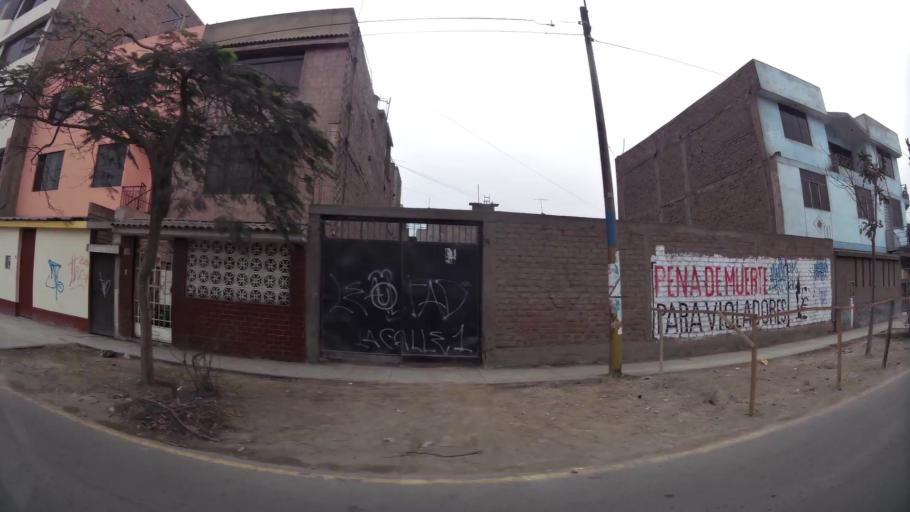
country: PE
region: Lima
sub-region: Lima
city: Independencia
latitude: -11.9736
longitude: -77.0012
